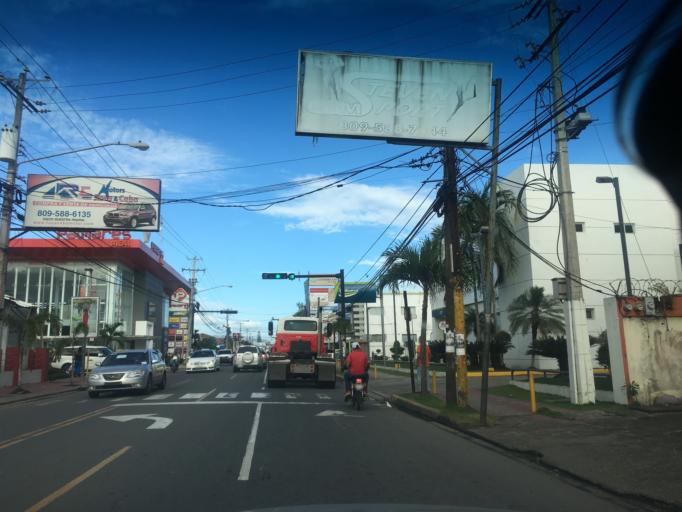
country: DO
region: Duarte
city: San Francisco de Macoris
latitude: 19.2871
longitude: -70.2700
